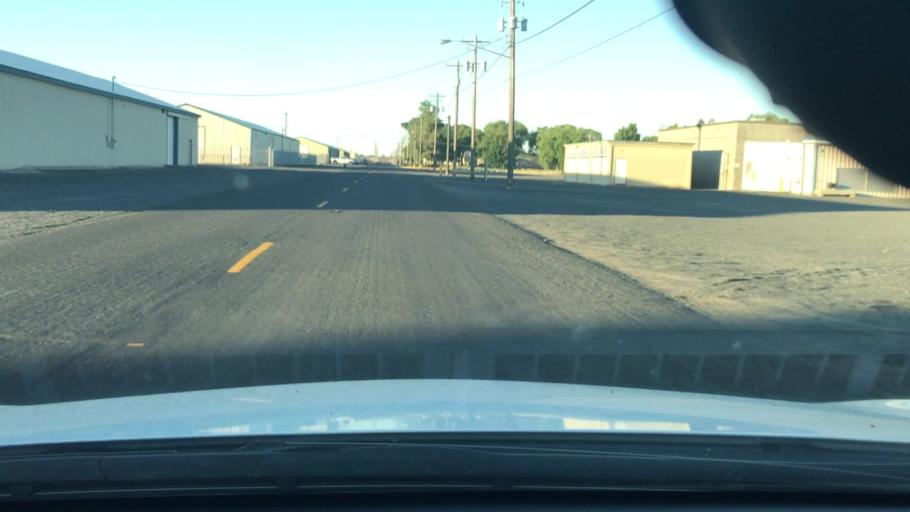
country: US
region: Washington
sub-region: Grant County
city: Moses Lake North
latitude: 47.1880
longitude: -119.3166
